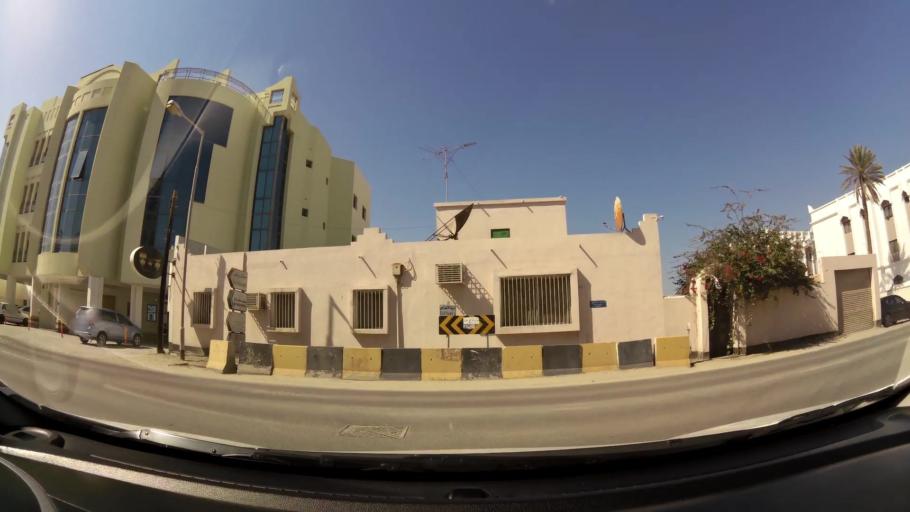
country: BH
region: Manama
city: Manama
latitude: 26.2065
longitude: 50.5788
